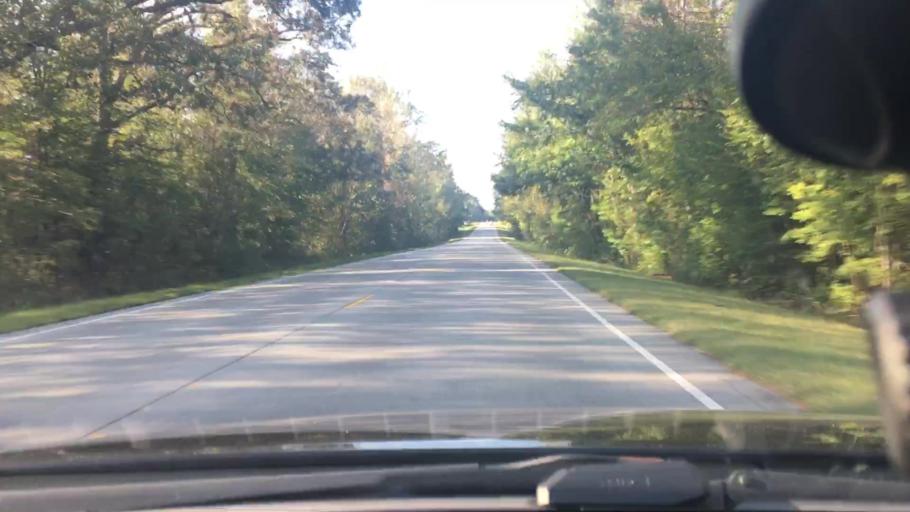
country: US
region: North Carolina
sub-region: Craven County
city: Vanceboro
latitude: 35.3118
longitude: -77.1395
